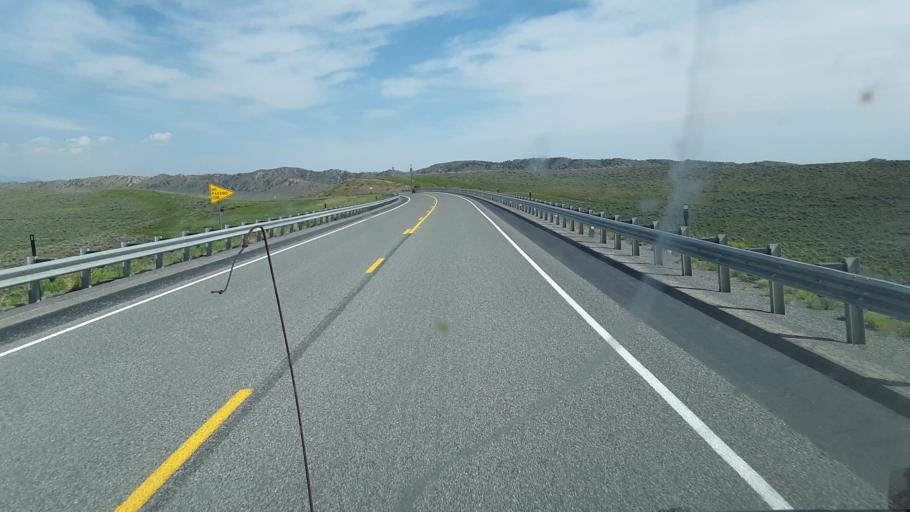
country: US
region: Wyoming
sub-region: Park County
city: Cody
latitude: 44.2673
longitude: -108.8724
